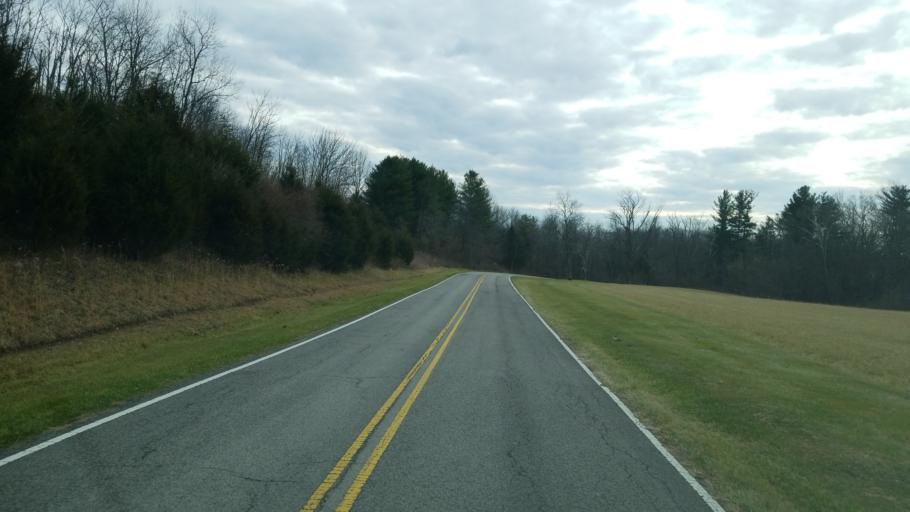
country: US
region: Ohio
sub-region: Highland County
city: Greenfield
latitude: 39.2428
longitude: -83.3891
